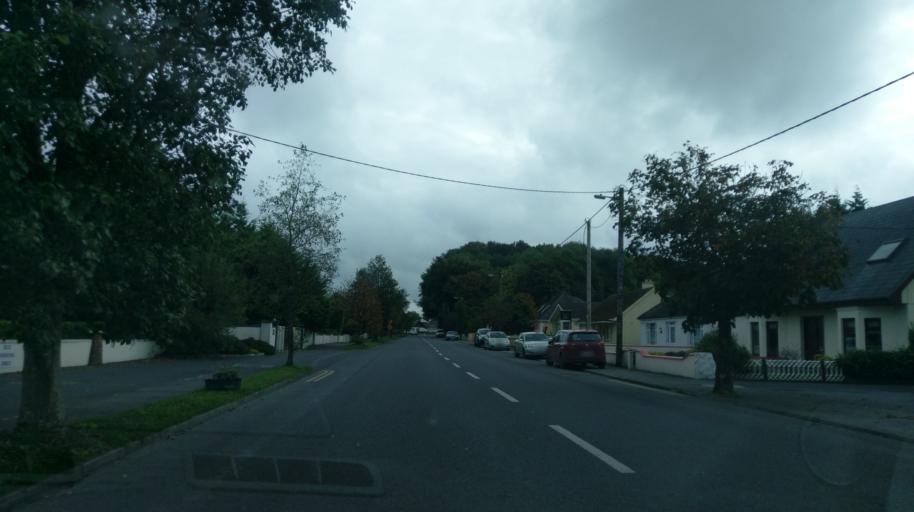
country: IE
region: Connaught
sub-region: County Galway
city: Loughrea
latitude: 53.4691
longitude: -8.4973
